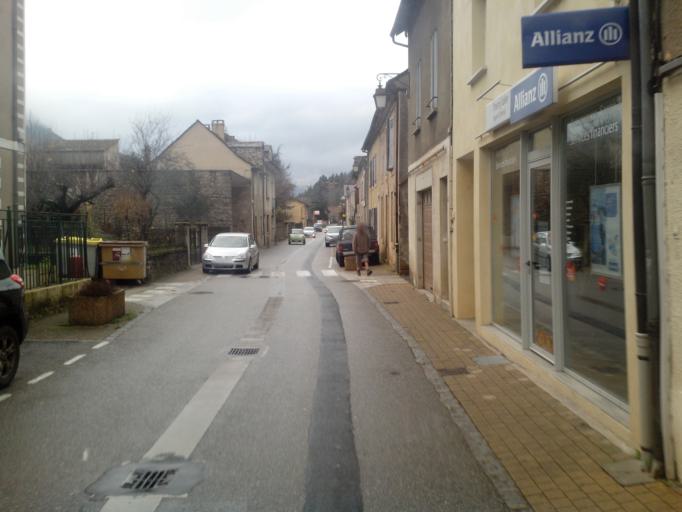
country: FR
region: Languedoc-Roussillon
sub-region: Departement de la Lozere
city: Florac
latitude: 44.3267
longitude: 3.5936
